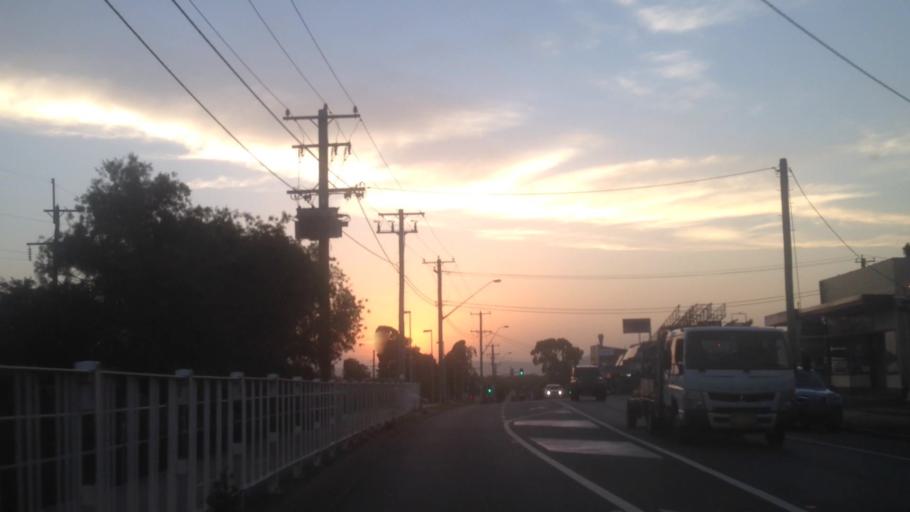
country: AU
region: New South Wales
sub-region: Lake Macquarie Shire
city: Dora Creek
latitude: -33.1074
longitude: 151.4908
